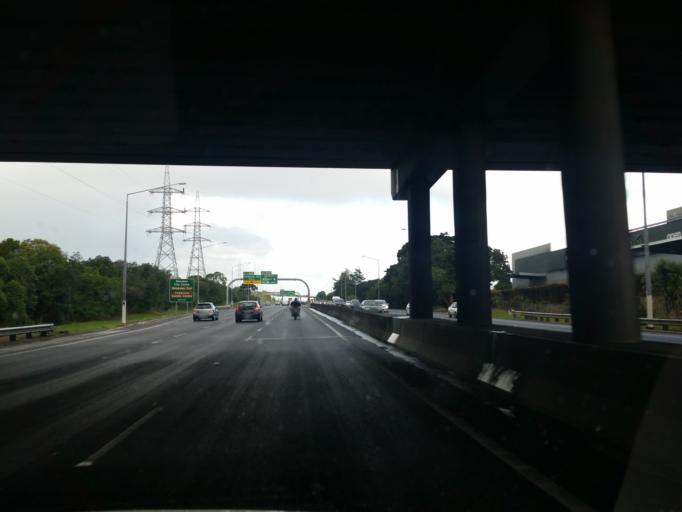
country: NZ
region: Auckland
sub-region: Auckland
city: Manukau City
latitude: -36.9856
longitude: 174.8846
